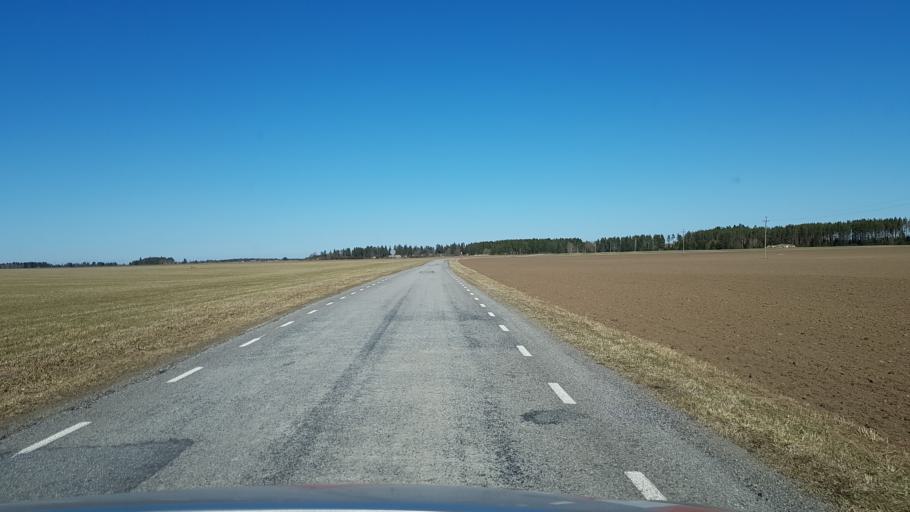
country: EE
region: Laeaene-Virumaa
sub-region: Someru vald
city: Someru
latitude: 59.4000
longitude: 26.5120
